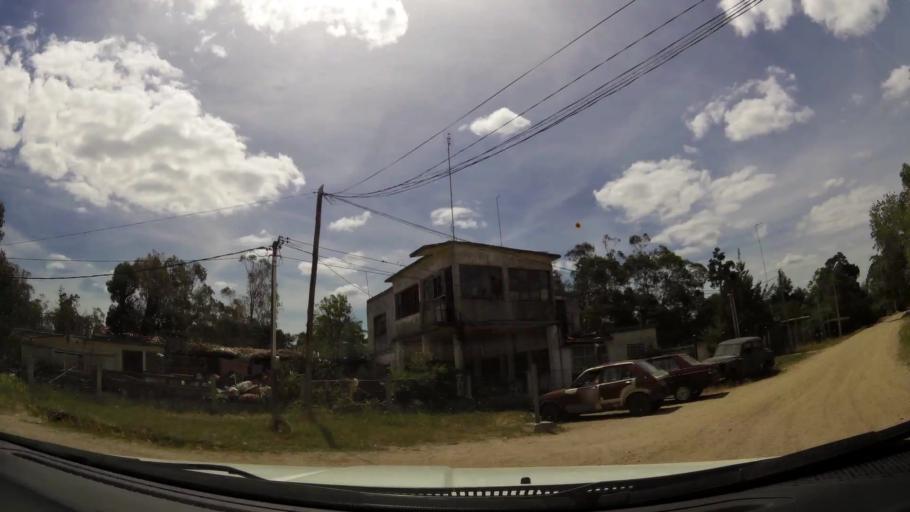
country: UY
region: San Jose
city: Delta del Tigre
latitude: -34.7512
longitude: -56.4579
